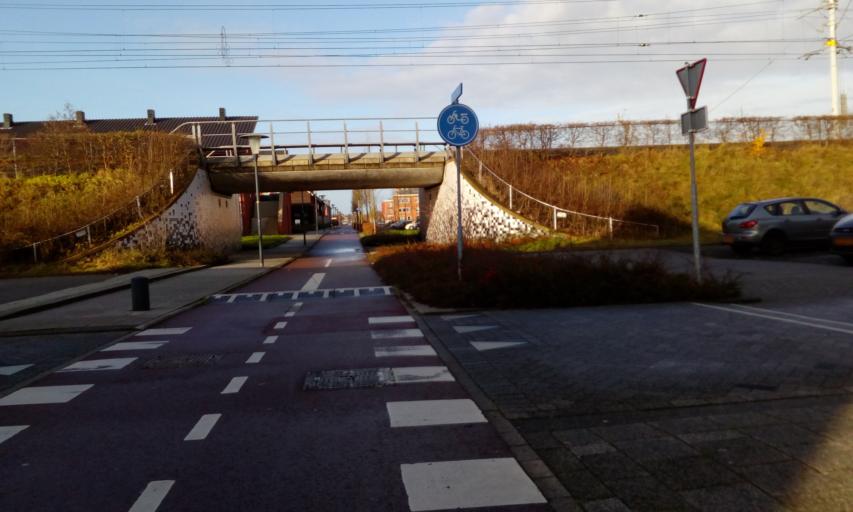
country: NL
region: South Holland
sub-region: Gemeente Rijnwoude
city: Benthuizen
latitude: 52.0557
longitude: 4.5408
